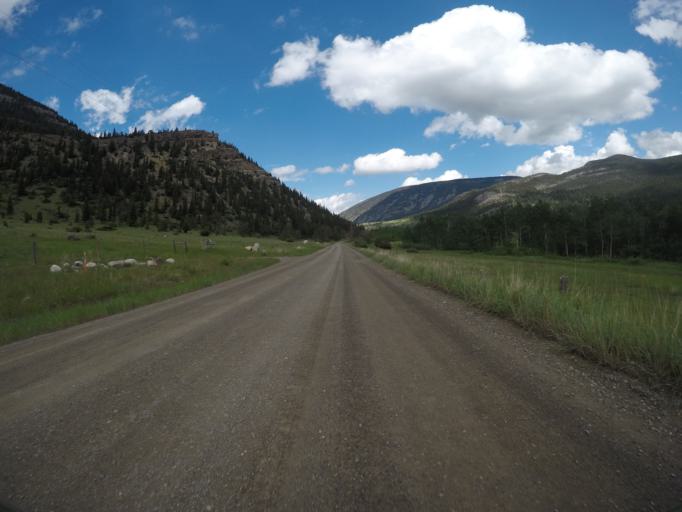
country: US
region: Montana
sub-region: Park County
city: Livingston
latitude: 45.5297
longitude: -110.2164
